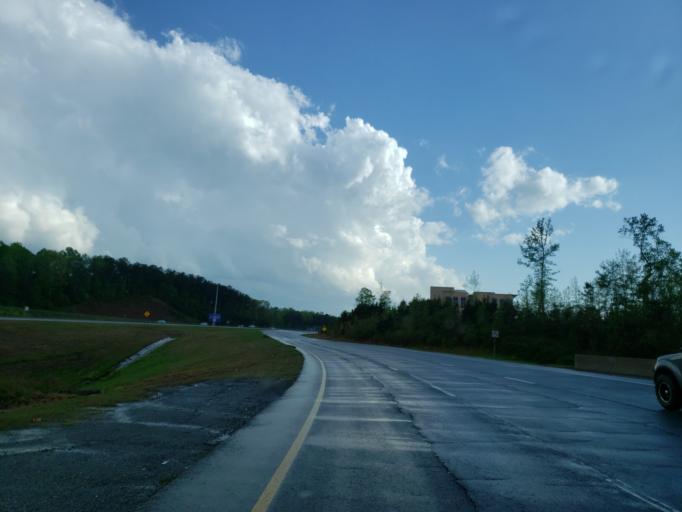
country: US
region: Georgia
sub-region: Cherokee County
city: Holly Springs
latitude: 34.1459
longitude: -84.5182
